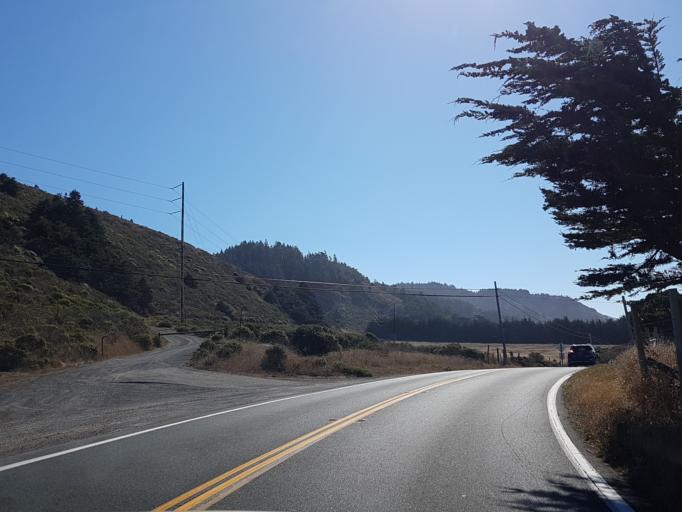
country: US
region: California
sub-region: Mendocino County
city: Boonville
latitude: 39.0988
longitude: -123.7056
